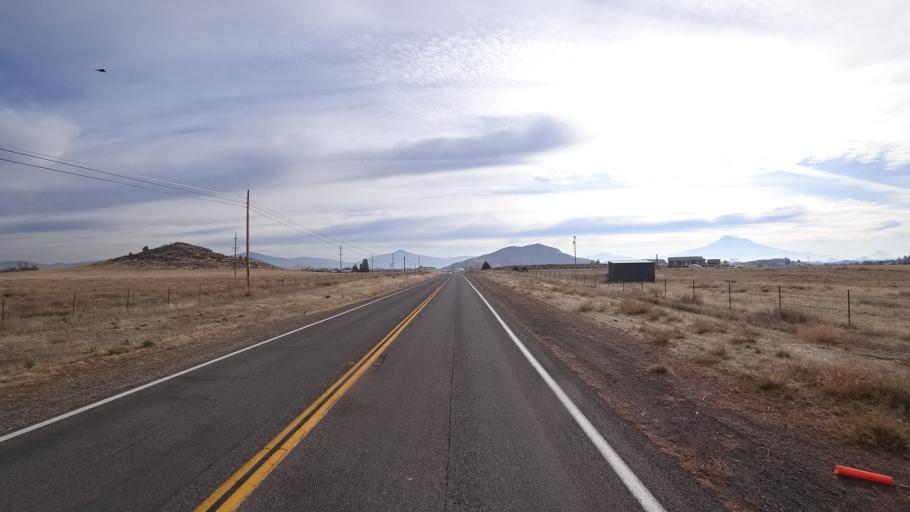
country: US
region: California
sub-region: Siskiyou County
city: Montague
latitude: 41.7248
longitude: -122.5501
